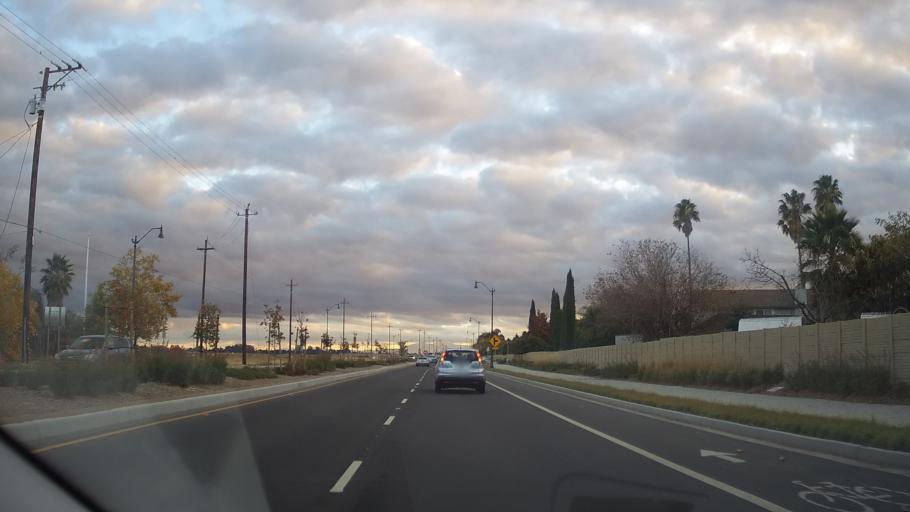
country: US
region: California
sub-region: Solano County
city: Vacaville
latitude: 38.3500
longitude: -121.9340
